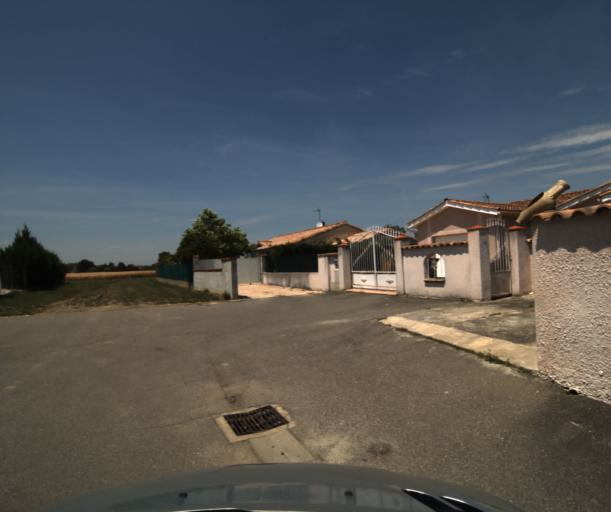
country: FR
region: Midi-Pyrenees
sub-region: Departement de la Haute-Garonne
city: Labastidette
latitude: 43.4654
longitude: 1.2461
